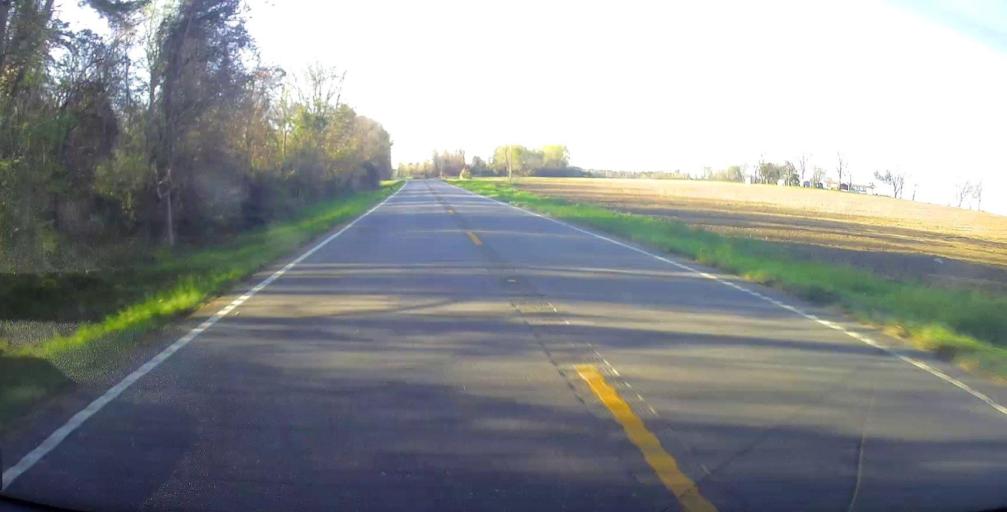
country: US
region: Georgia
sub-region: Pulaski County
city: Hawkinsville
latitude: 32.2174
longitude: -83.3855
